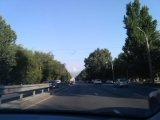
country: KZ
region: Almaty Qalasy
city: Almaty
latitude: 43.2268
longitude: 76.8453
